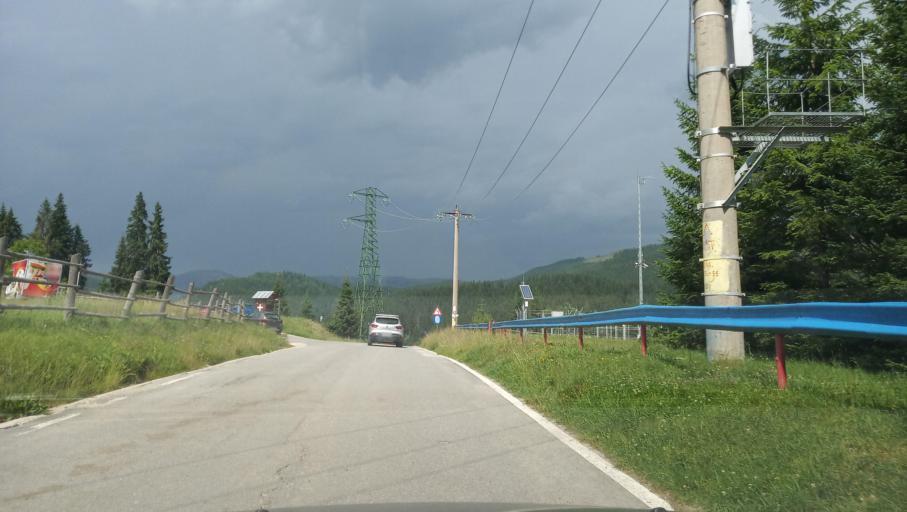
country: RO
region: Dambovita
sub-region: Comuna Moroeni
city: Glod
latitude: 45.3406
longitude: 25.4259
